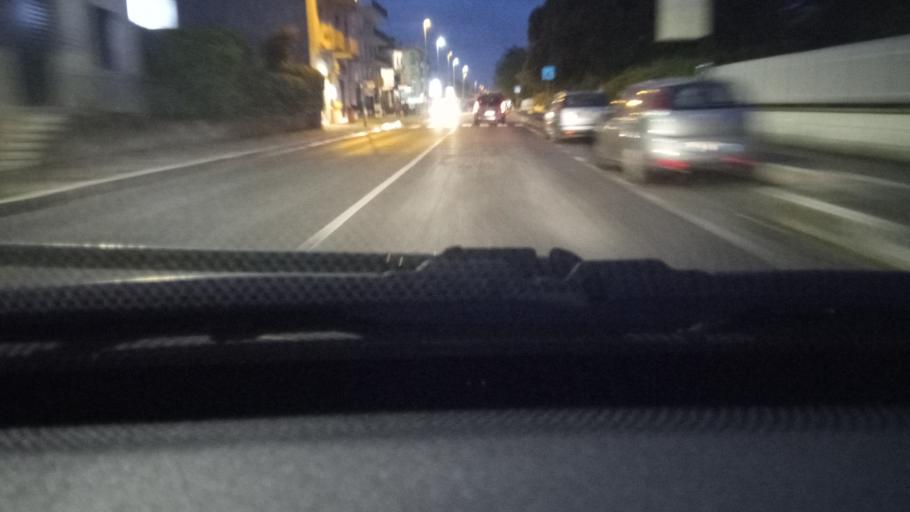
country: IT
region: Latium
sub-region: Provincia di Latina
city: Formia
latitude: 41.2618
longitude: 13.6324
